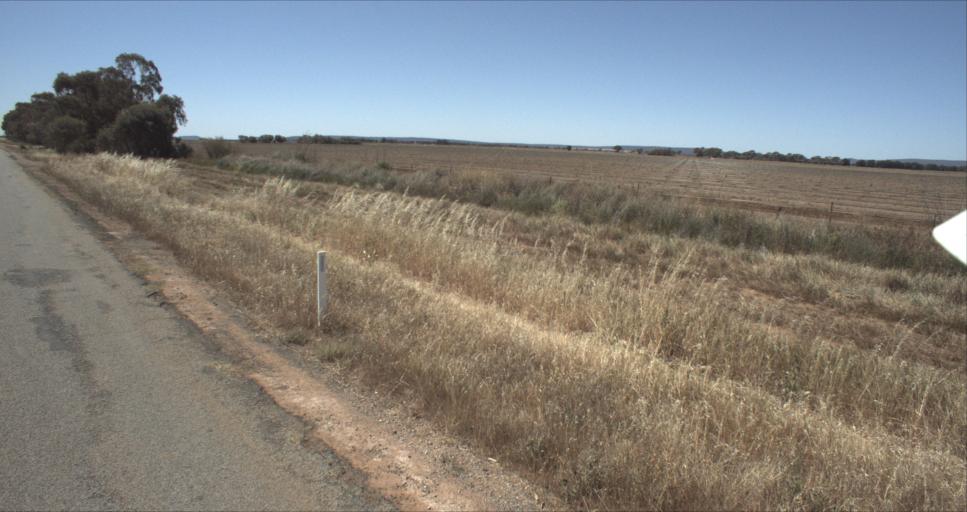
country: AU
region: New South Wales
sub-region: Leeton
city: Leeton
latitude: -34.5157
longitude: 146.3452
